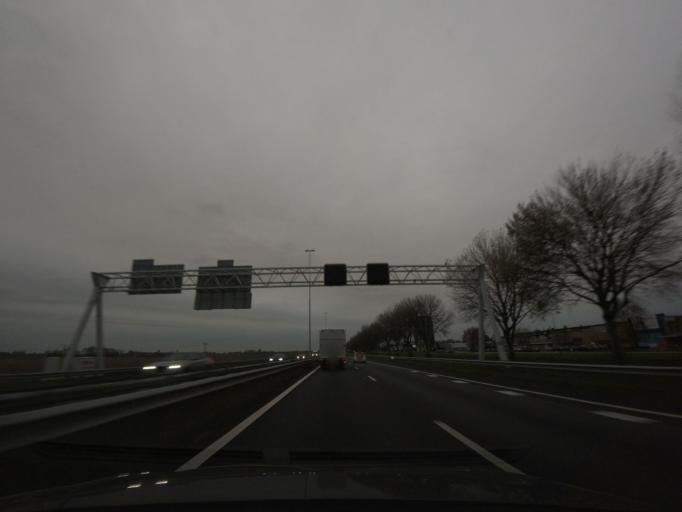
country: NL
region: North Brabant
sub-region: Gemeente Geertruidenberg
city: Geertruidenberg
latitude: 51.7102
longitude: 4.8888
